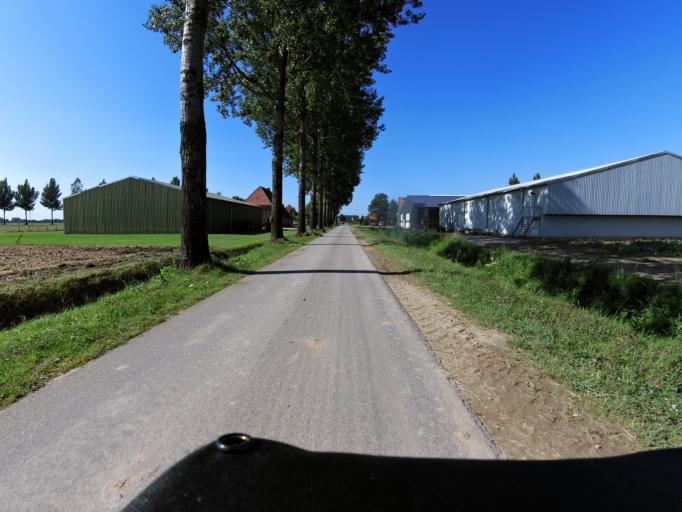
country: NL
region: South Holland
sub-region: Gemeente Dordrecht
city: Dordrecht
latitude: 51.7658
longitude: 4.7151
